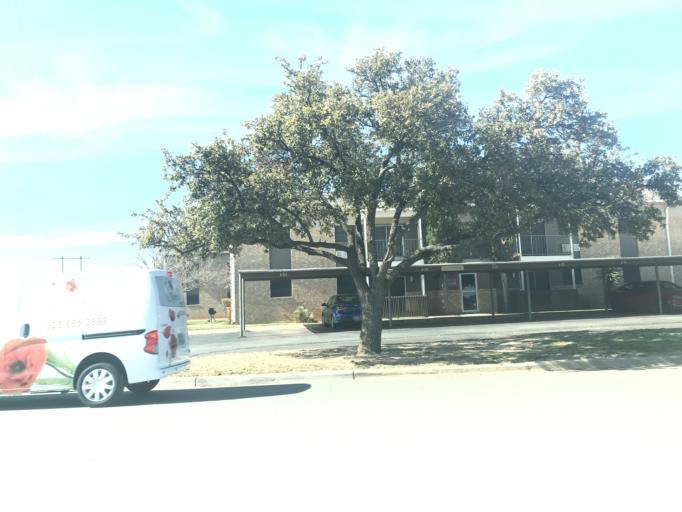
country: US
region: Texas
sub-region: Tom Green County
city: San Angelo
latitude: 31.4304
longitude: -100.4846
